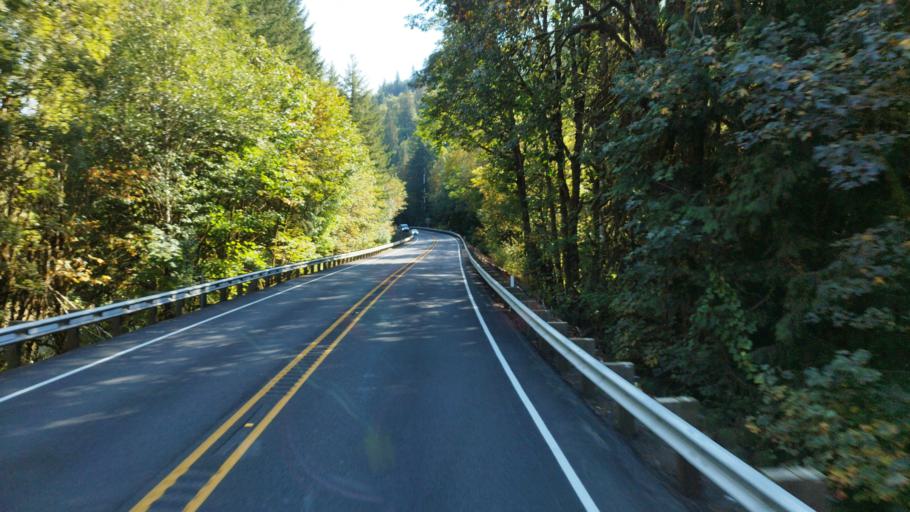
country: US
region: Oregon
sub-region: Columbia County
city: Vernonia
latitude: 45.8622
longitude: -123.5630
